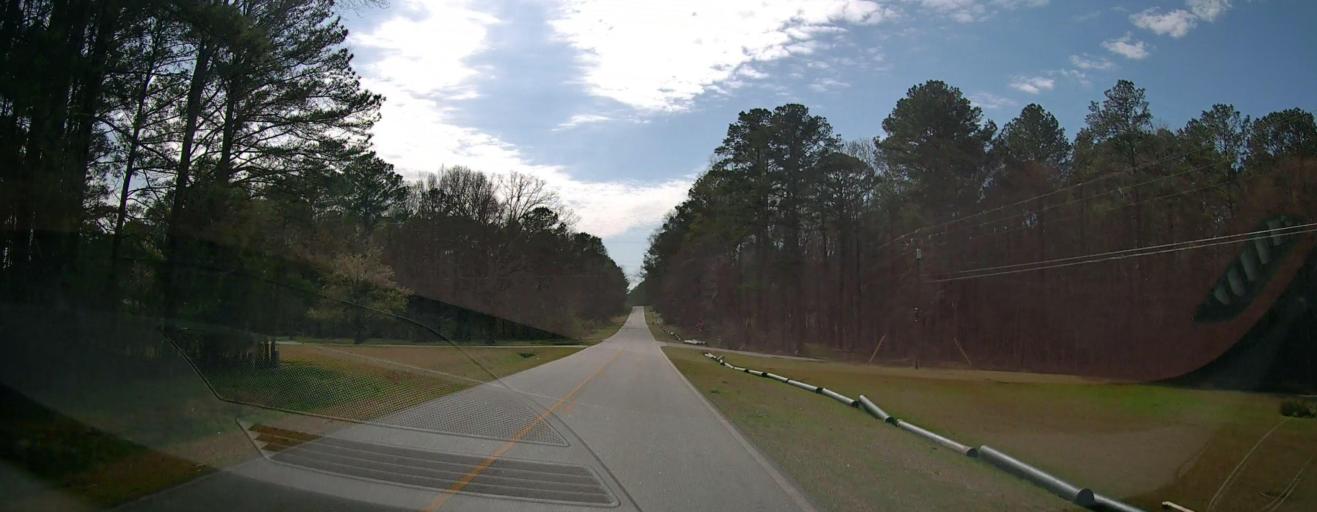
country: US
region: Georgia
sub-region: Monroe County
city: Forsyth
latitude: 33.1027
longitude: -83.8233
